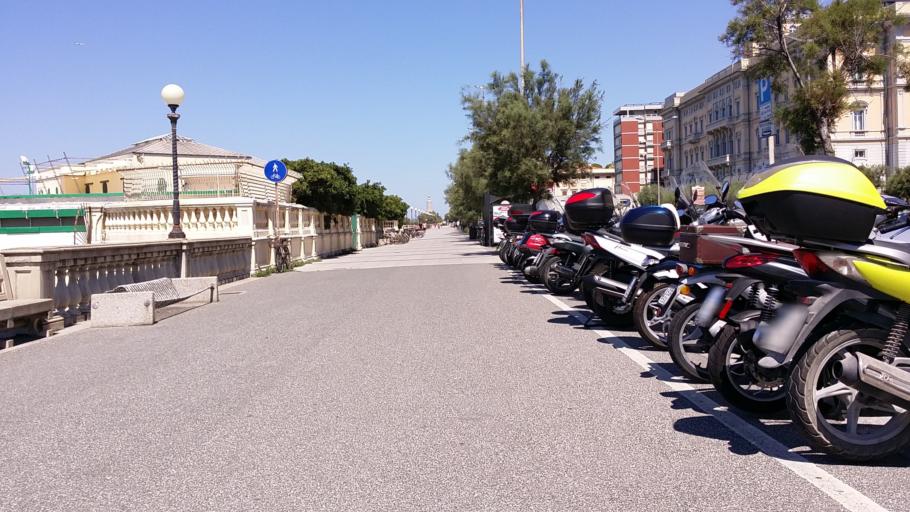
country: IT
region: Tuscany
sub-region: Provincia di Livorno
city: Livorno
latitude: 43.5315
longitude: 10.3029
